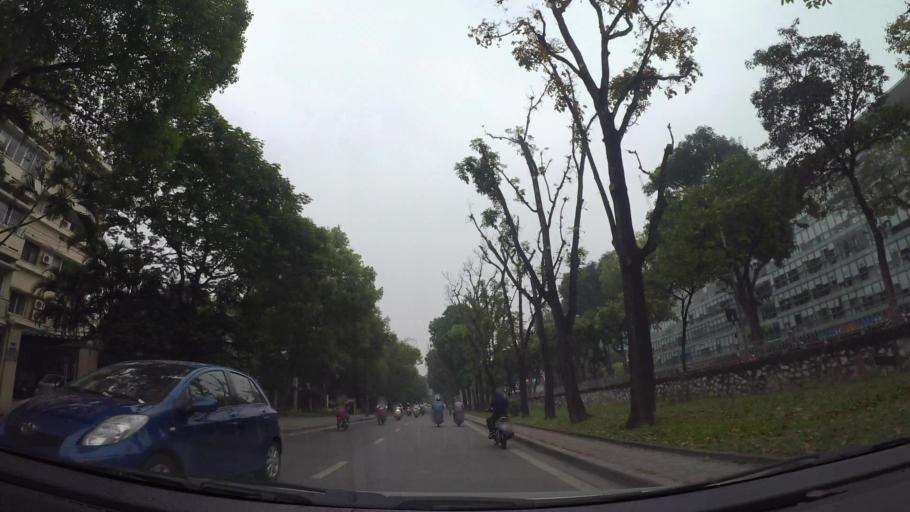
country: VN
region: Ha Noi
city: Dong Da
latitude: 21.0312
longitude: 105.8196
